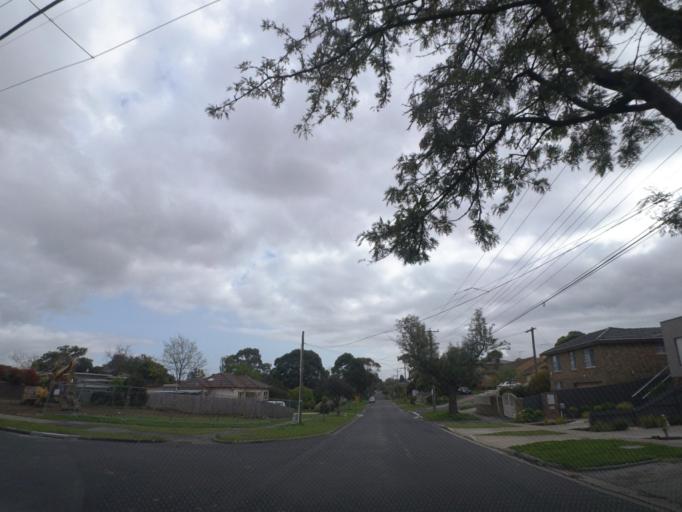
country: AU
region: Victoria
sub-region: Whitehorse
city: Nunawading
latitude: -37.8136
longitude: 145.1853
